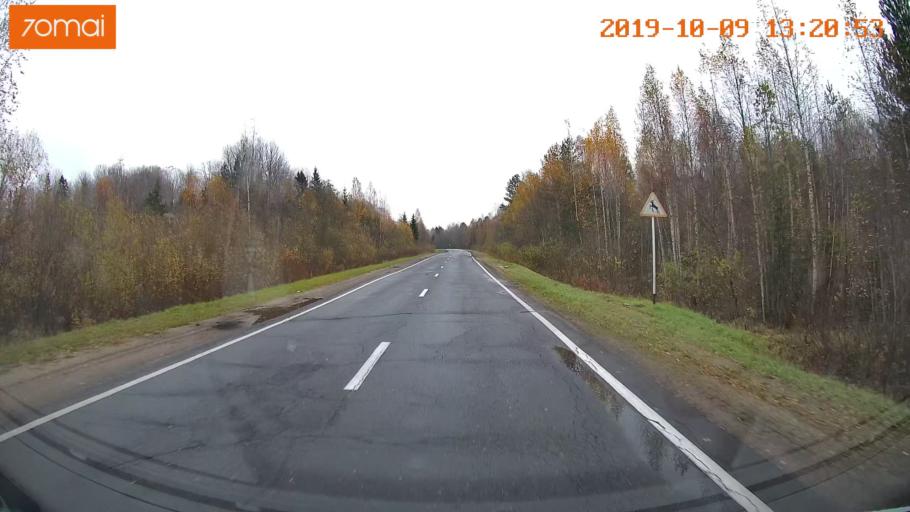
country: RU
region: Jaroslavl
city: Lyubim
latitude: 58.3416
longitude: 40.8367
